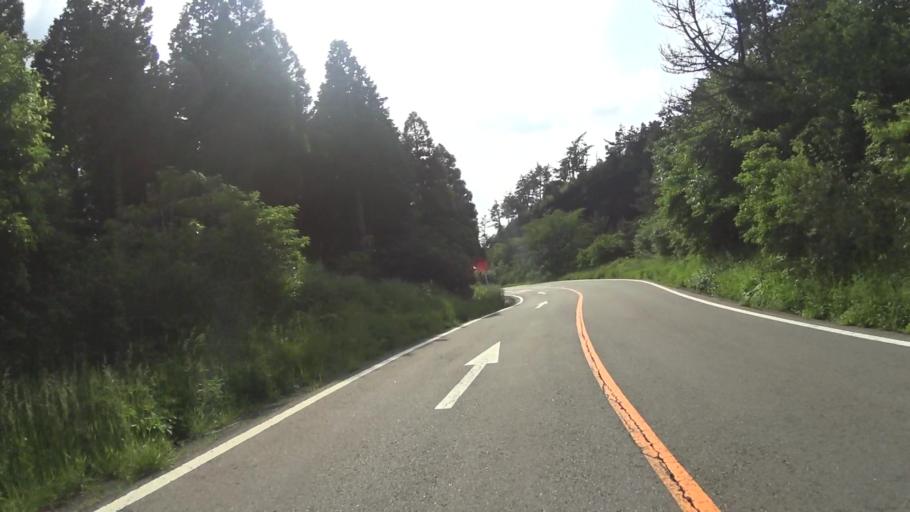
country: JP
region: Kumamoto
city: Aso
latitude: 32.8977
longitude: 131.0488
